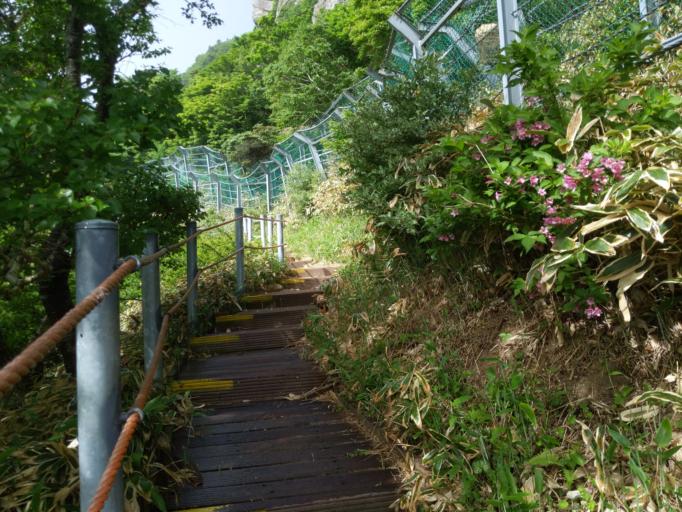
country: KR
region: Jeju-do
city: Seogwipo
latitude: 33.3751
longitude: 126.5301
